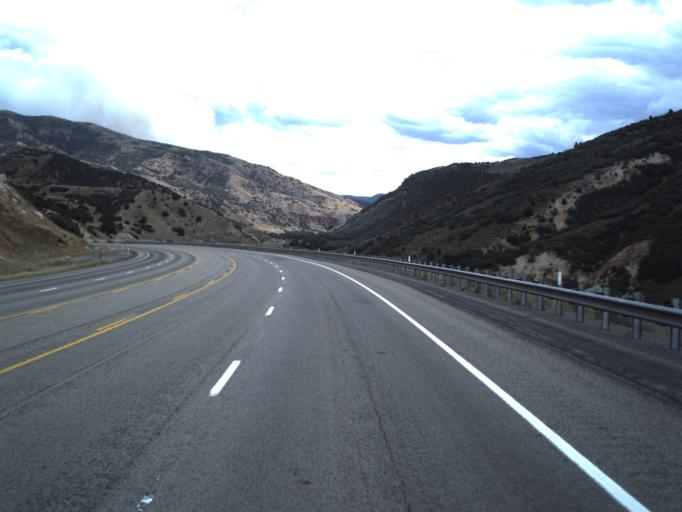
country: US
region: Utah
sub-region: Utah County
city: Mapleton
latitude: 39.9948
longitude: -111.4539
